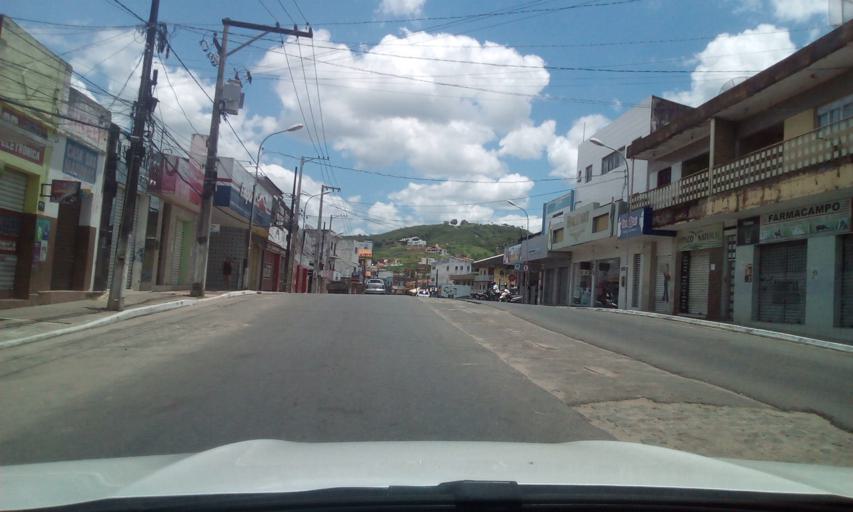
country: BR
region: Paraiba
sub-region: Guarabira
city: Guarabira
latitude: -6.8515
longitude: -35.4928
